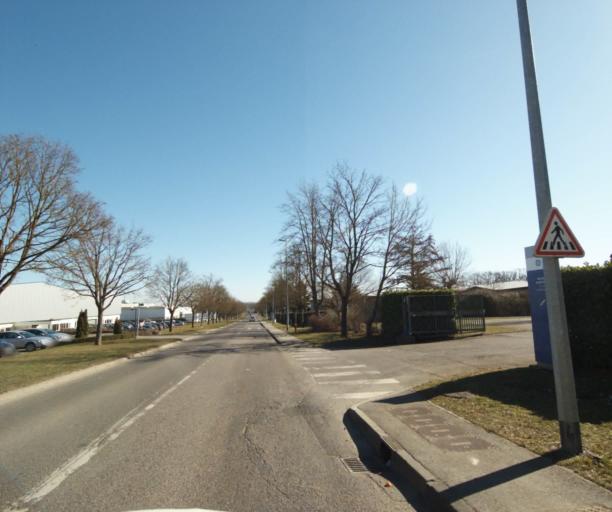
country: FR
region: Lorraine
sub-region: Departement de Meurthe-et-Moselle
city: Richardmenil
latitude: 48.6127
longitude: 6.1839
